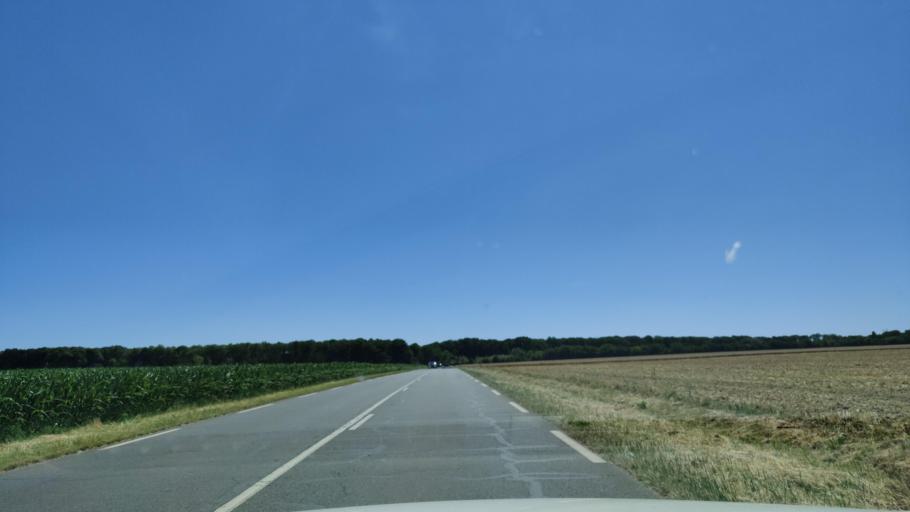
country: FR
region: Ile-de-France
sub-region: Departement de l'Essonne
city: Fontenay-les-Briis
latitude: 48.6363
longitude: 2.1807
